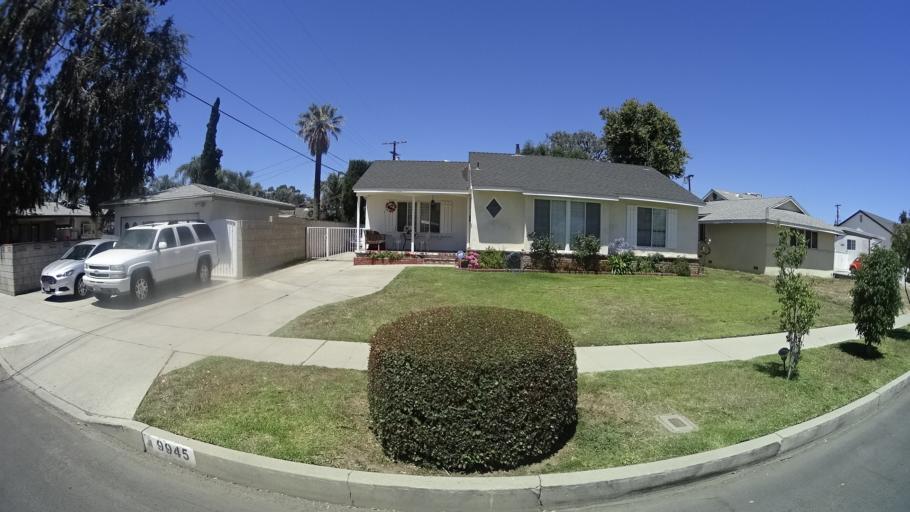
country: US
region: California
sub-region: Los Angeles County
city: San Fernando
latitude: 34.2515
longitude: -118.4708
